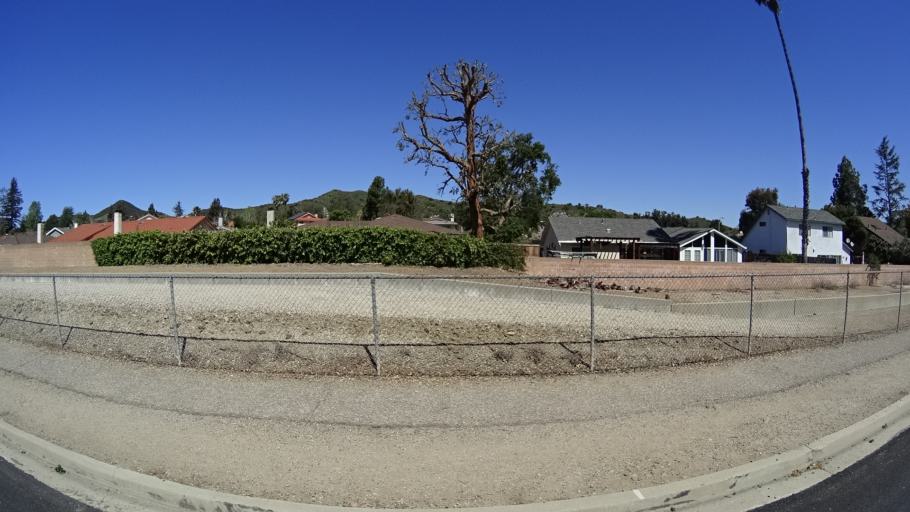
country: US
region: California
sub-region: Ventura County
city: Casa Conejo
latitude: 34.1581
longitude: -118.9603
